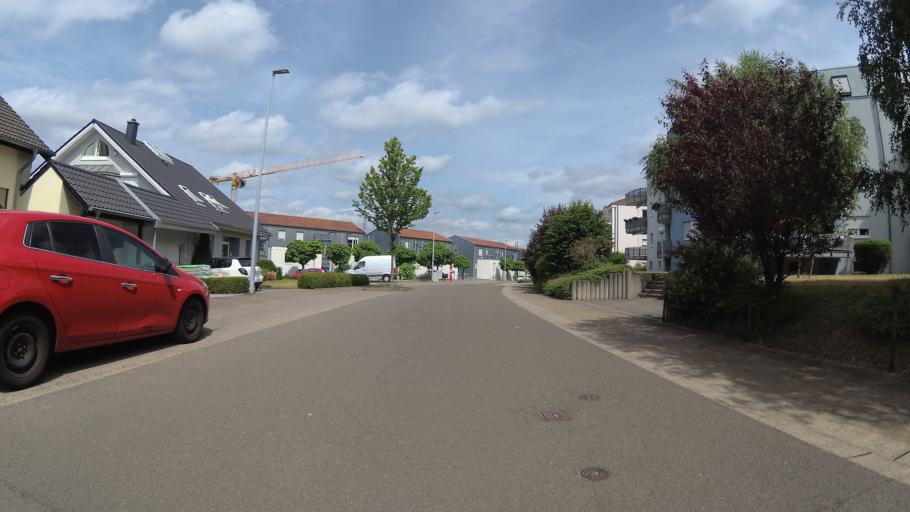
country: DE
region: Saarland
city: Sankt Ingbert
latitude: 49.2798
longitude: 7.1258
